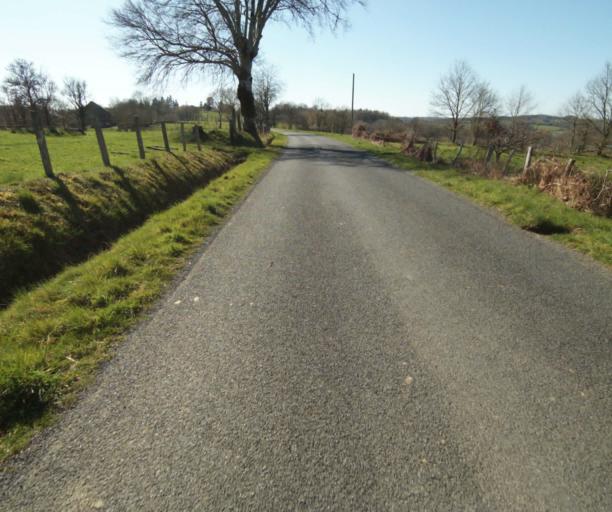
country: FR
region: Limousin
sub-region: Departement de la Correze
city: Chamboulive
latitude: 45.4287
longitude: 1.6537
